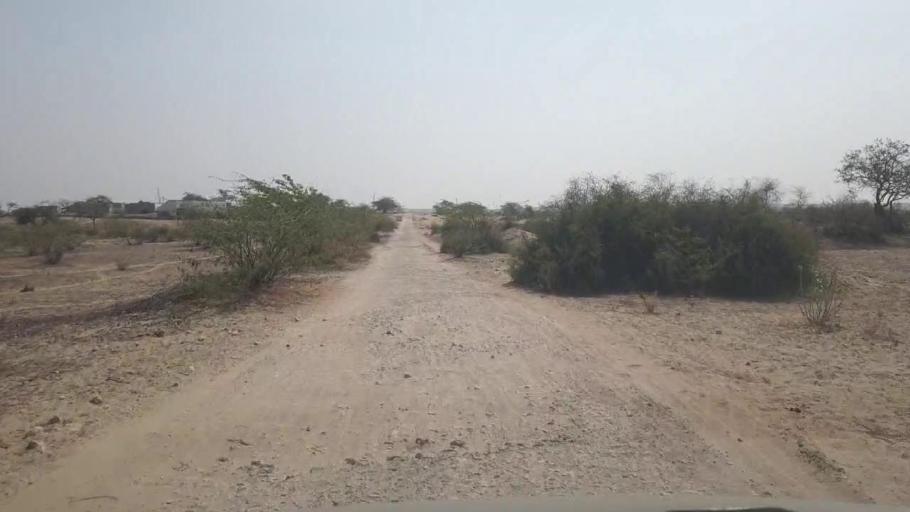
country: PK
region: Sindh
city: Chor
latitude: 25.4591
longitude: 69.7863
